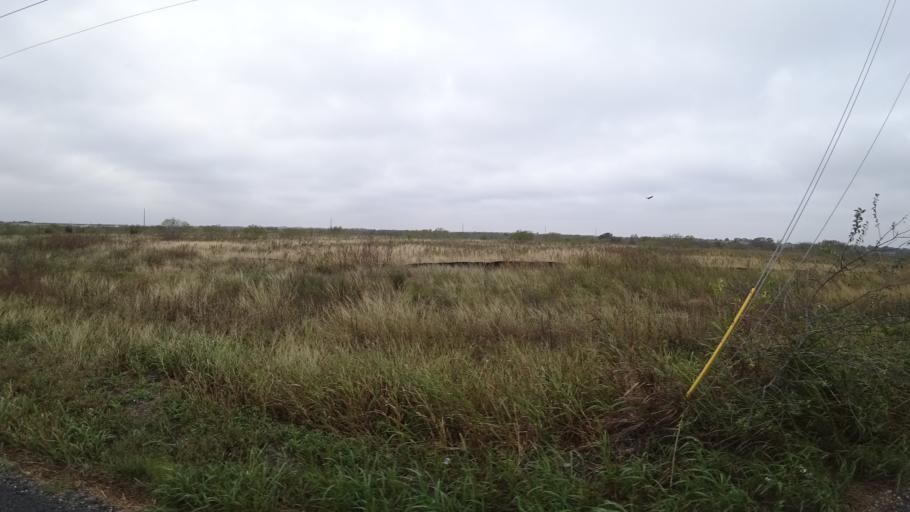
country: US
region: Texas
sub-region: Travis County
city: Pflugerville
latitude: 30.4144
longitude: -97.6097
